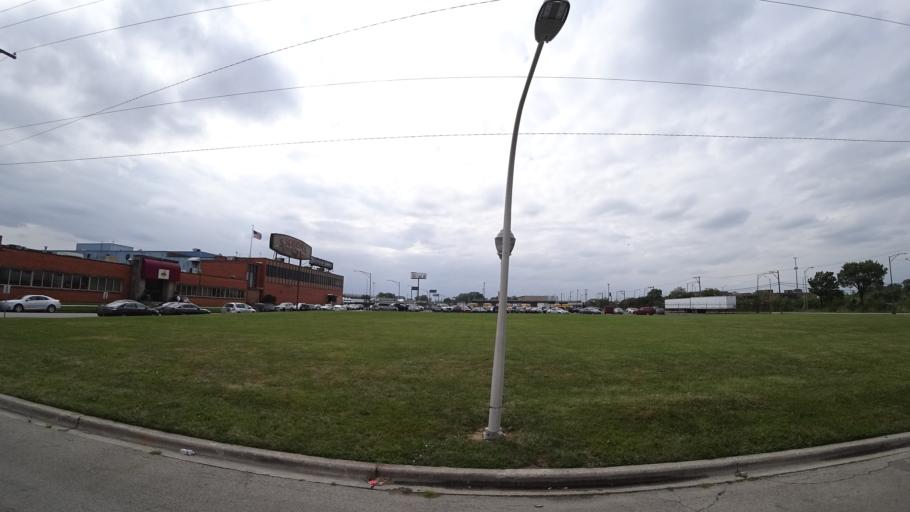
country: US
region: Illinois
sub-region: Cook County
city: Cicero
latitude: 41.8705
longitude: -87.7490
